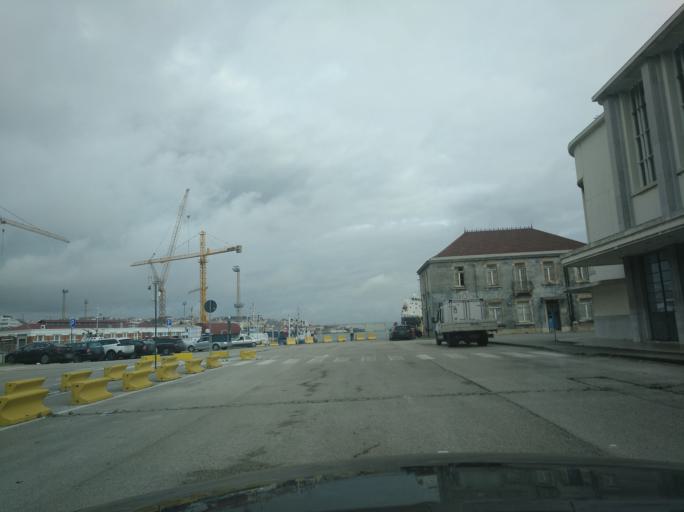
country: PT
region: Setubal
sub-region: Almada
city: Cacilhas
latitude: 38.7018
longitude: -9.1621
